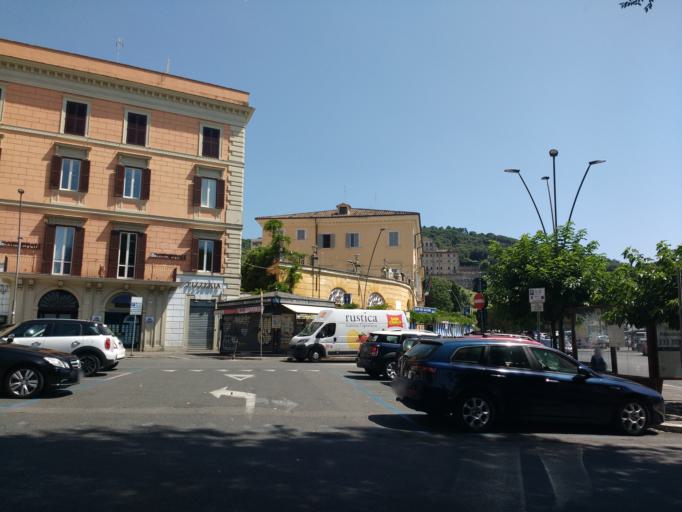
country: IT
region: Latium
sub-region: Citta metropolitana di Roma Capitale
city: Armetta
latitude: 41.8068
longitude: 12.6798
